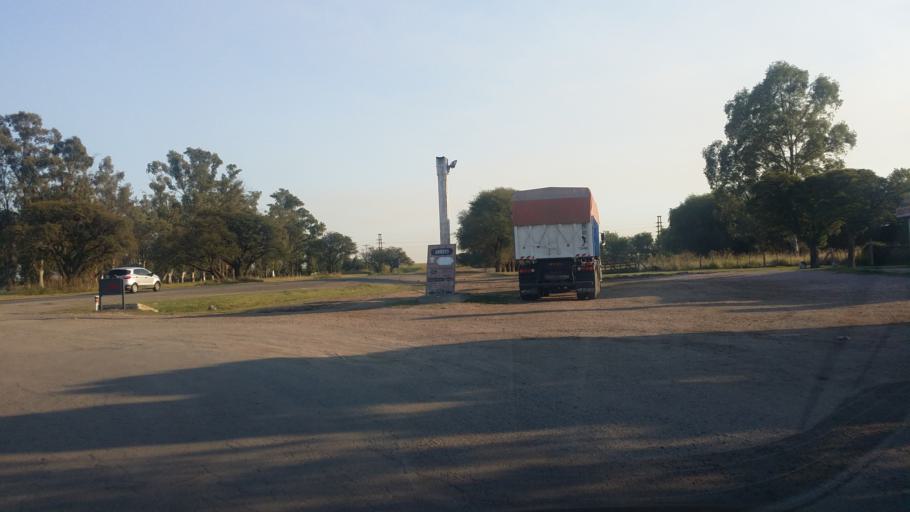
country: AR
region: La Pampa
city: Winifreda
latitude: -36.2223
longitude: -64.2779
